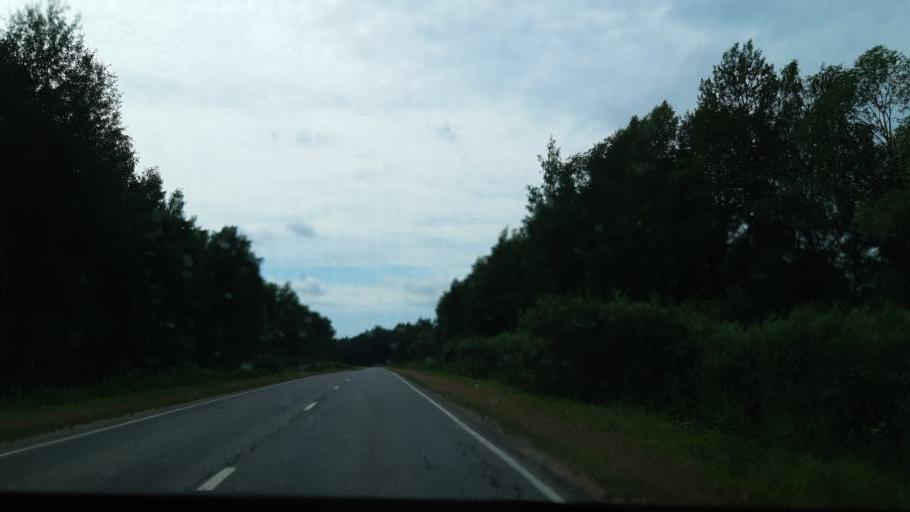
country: RU
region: Moskovskaya
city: Vereya
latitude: 55.3706
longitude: 36.2336
